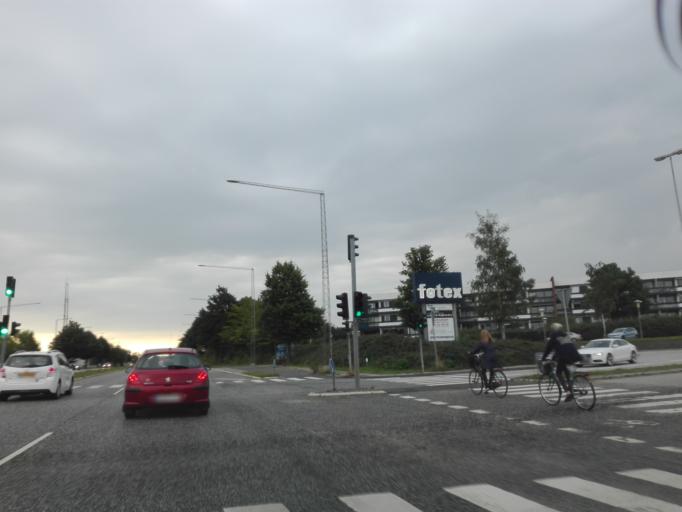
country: DK
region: Central Jutland
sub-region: Arhus Kommune
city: Lystrup
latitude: 56.2057
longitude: 10.2627
